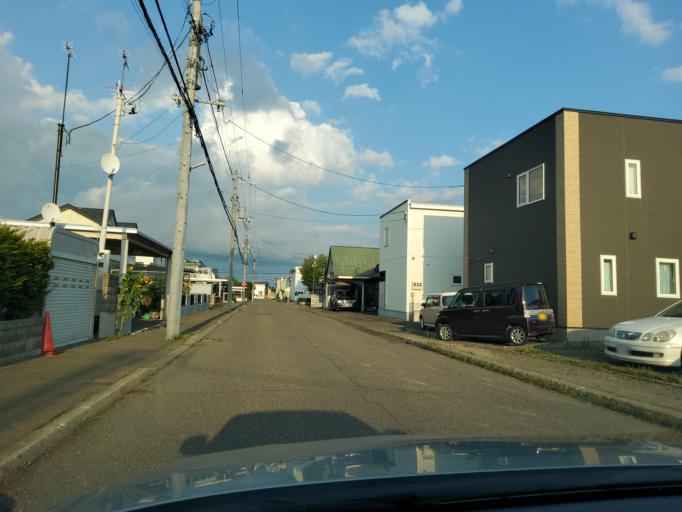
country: JP
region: Hokkaido
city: Obihiro
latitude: 42.9197
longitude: 143.1545
